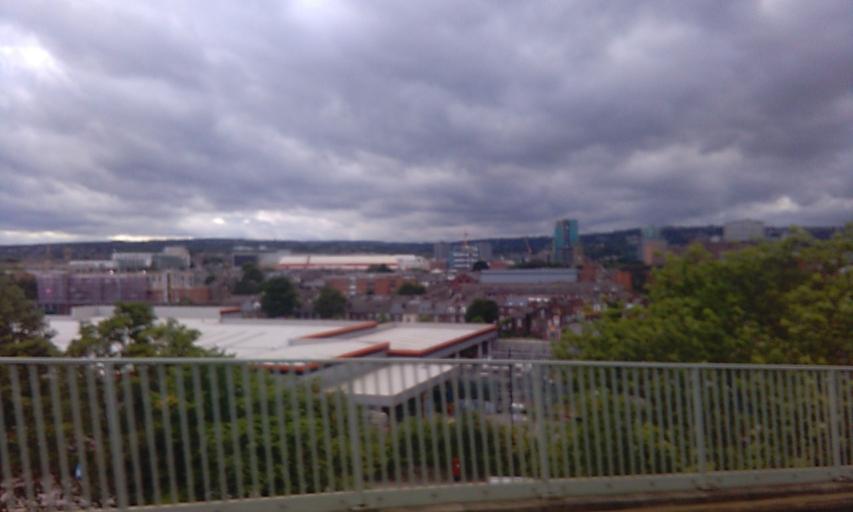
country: GB
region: England
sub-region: Sheffield
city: Sheffield
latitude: 53.3716
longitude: -1.4610
